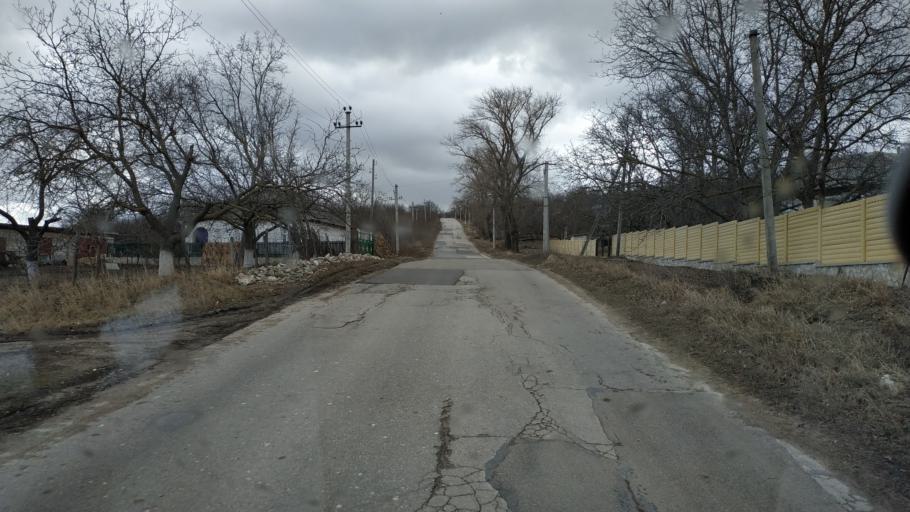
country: MD
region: Stinga Nistrului
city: Bucovat
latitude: 47.2259
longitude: 28.4261
